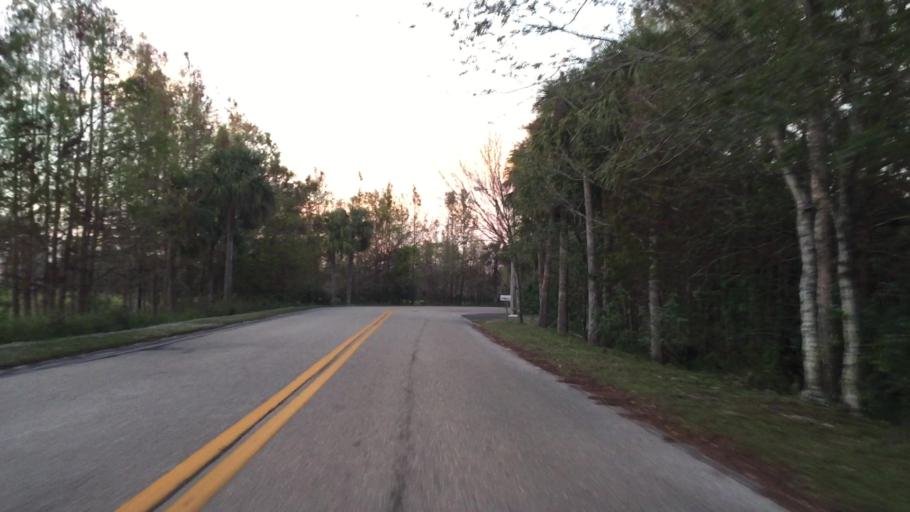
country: US
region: Florida
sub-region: Lee County
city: Gateway
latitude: 26.5381
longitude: -81.7915
